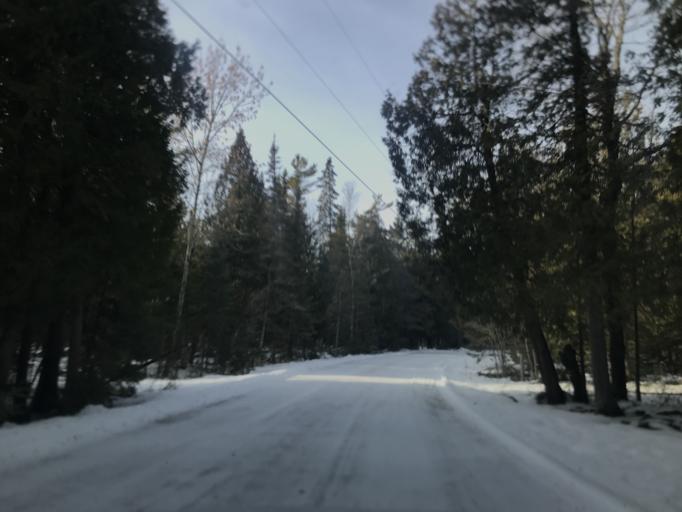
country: US
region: Wisconsin
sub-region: Door County
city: Sturgeon Bay
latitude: 45.1412
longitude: -87.0502
